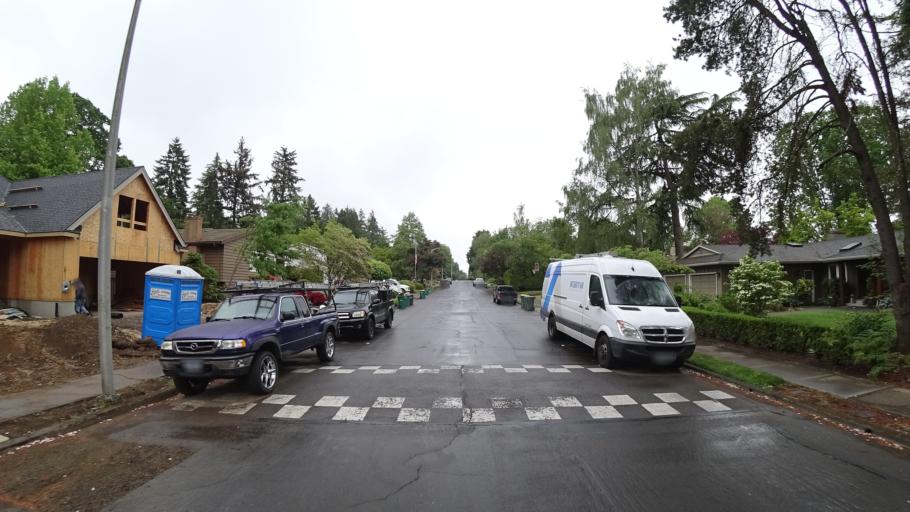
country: US
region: Oregon
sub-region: Washington County
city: Raleigh Hills
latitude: 45.4773
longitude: -122.7726
